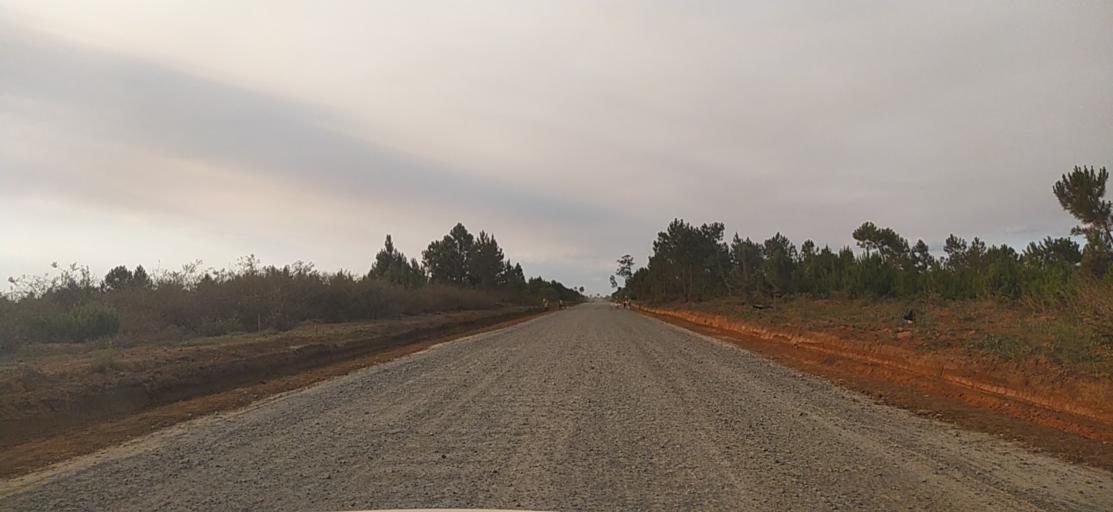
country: MG
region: Alaotra Mangoro
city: Moramanga
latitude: -18.5410
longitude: 48.2593
